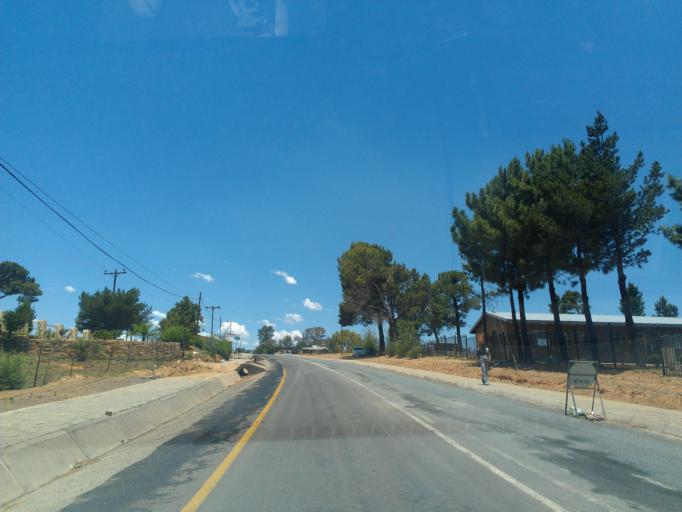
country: LS
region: Berea
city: Teyateyaneng
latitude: -29.1136
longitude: 27.9681
